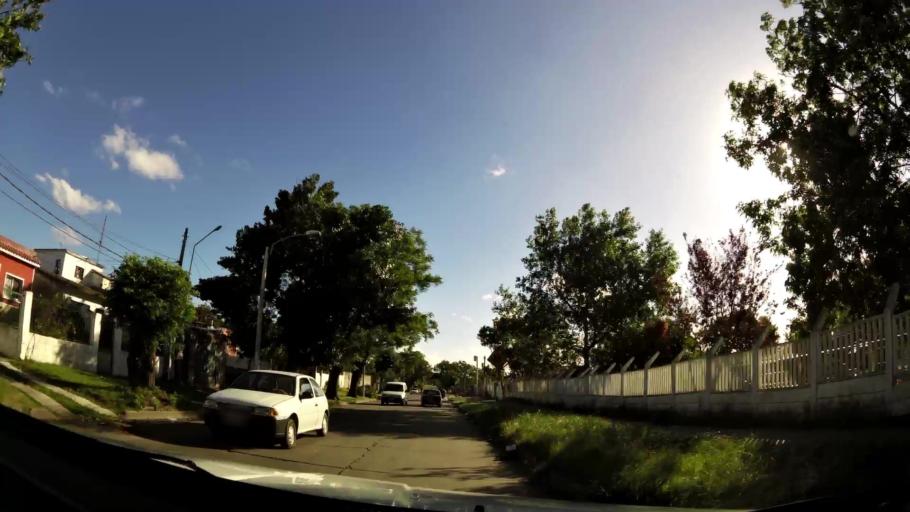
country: UY
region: Montevideo
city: Montevideo
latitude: -34.8457
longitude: -56.2460
